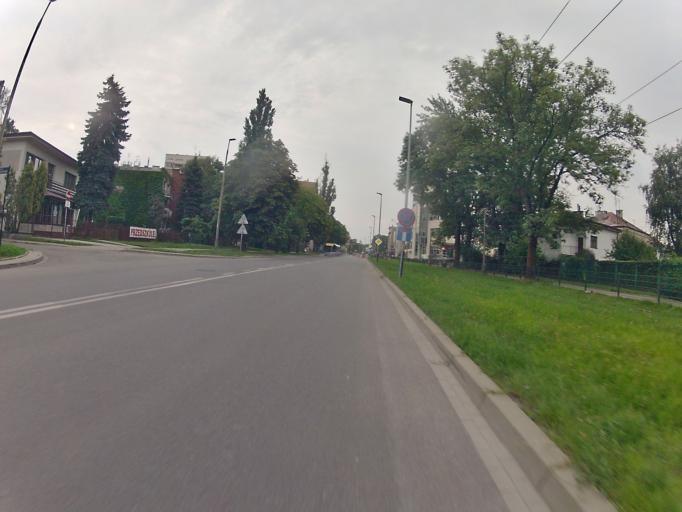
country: PL
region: Lesser Poland Voivodeship
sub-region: Krakow
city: Krakow
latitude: 50.0787
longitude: 19.8985
